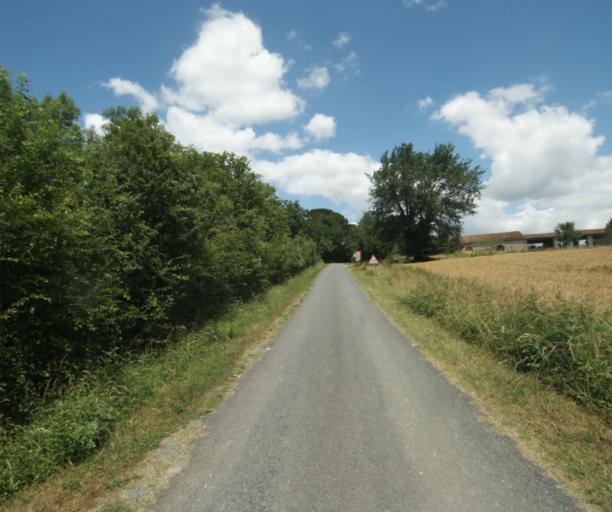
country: FR
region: Midi-Pyrenees
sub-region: Departement du Tarn
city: Puylaurens
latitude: 43.5236
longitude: 2.0244
